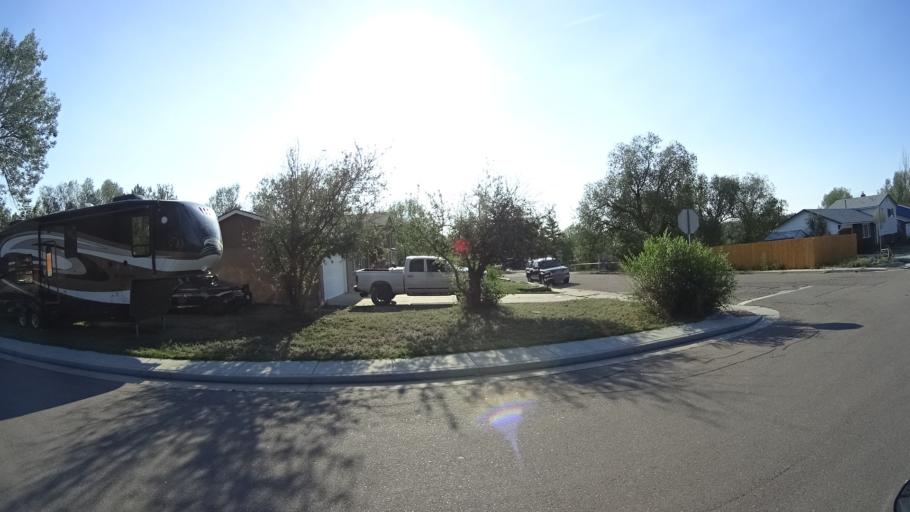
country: US
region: Colorado
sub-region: El Paso County
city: Stratmoor
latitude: 38.7746
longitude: -104.7969
